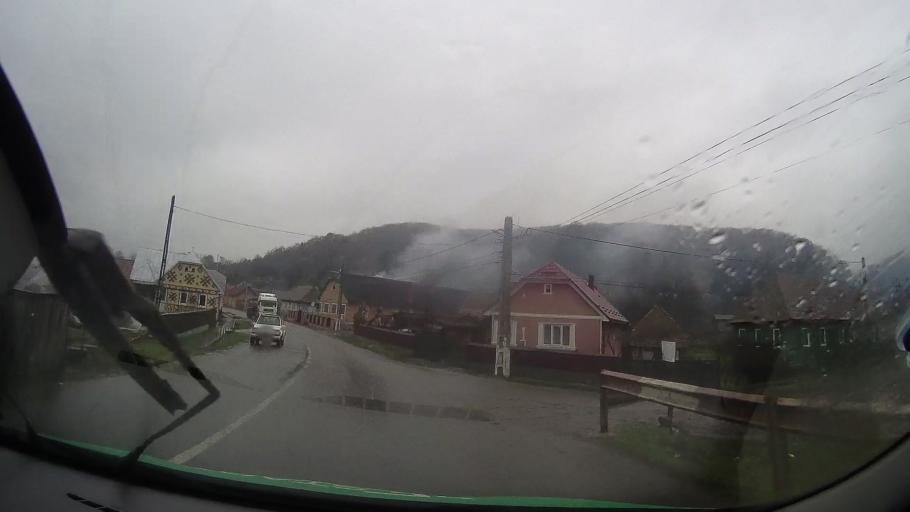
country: RO
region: Bistrita-Nasaud
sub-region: Comuna Sieut
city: Sieut
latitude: 46.9773
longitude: 24.6466
